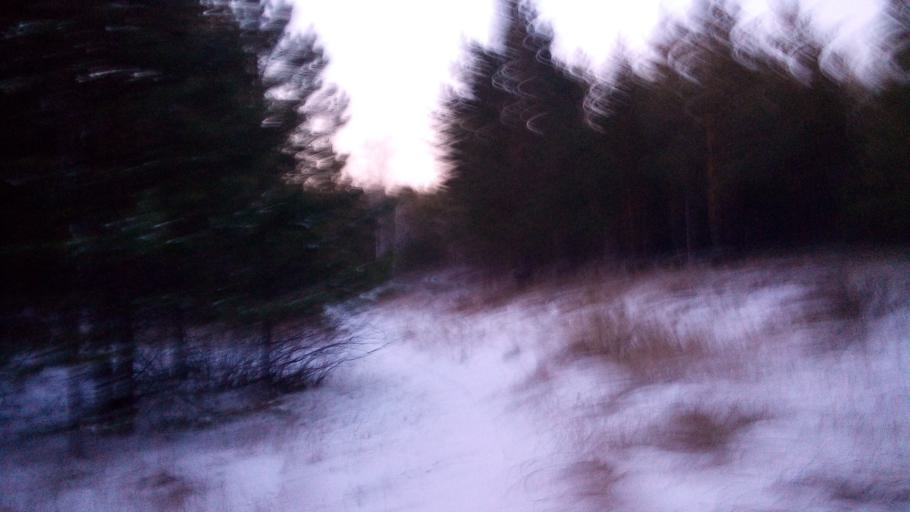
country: RU
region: Chelyabinsk
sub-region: Gorod Chelyabinsk
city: Chelyabinsk
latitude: 55.1624
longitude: 61.3331
